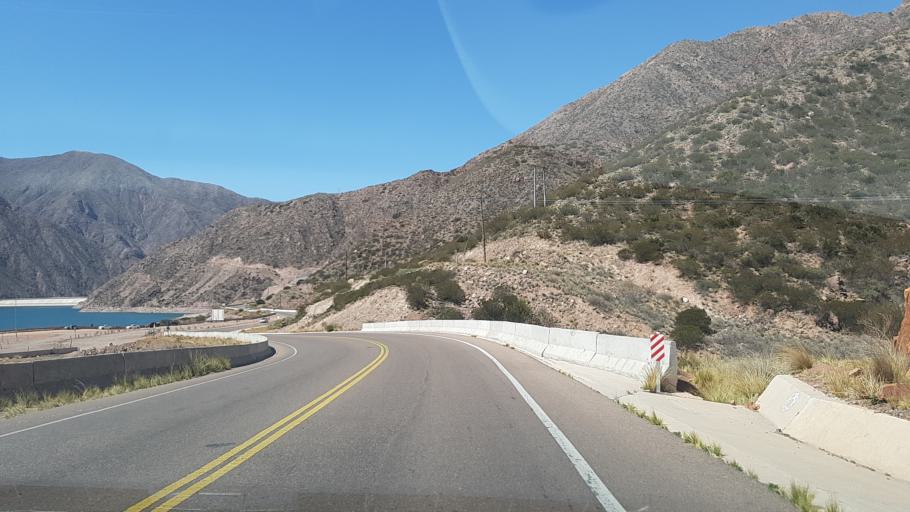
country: AR
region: Mendoza
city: Lujan de Cuyo
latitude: -32.9951
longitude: -69.1471
